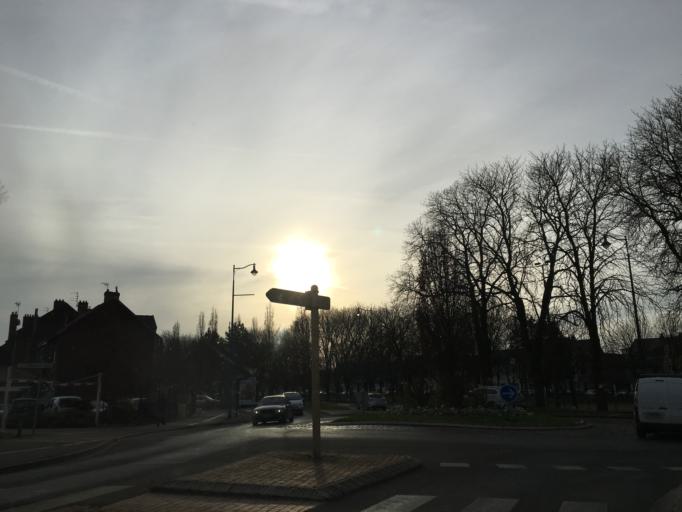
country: FR
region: Nord-Pas-de-Calais
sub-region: Departement du Pas-de-Calais
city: Arras
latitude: 50.2874
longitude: 2.7863
